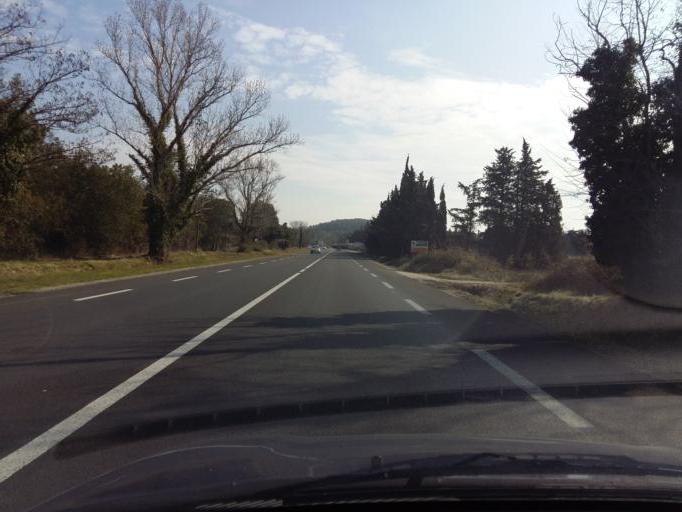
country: FR
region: Provence-Alpes-Cote d'Azur
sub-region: Departement des Bouches-du-Rhone
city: Orgon
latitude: 43.7954
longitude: 5.0147
